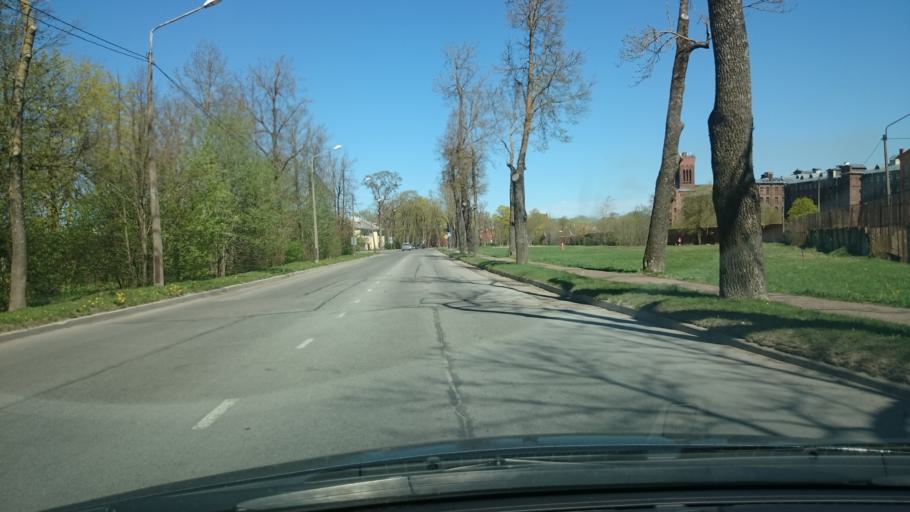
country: EE
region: Ida-Virumaa
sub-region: Narva linn
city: Narva
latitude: 59.3575
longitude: 28.1853
